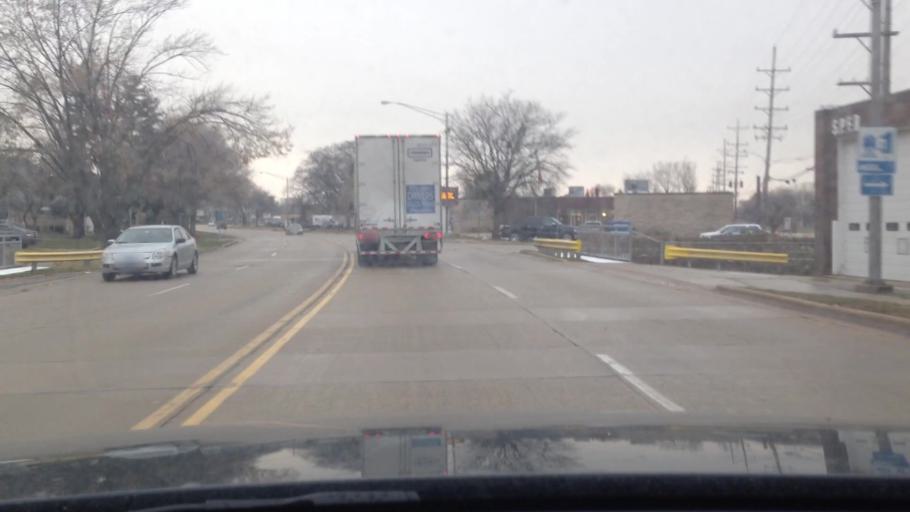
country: US
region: Illinois
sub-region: Cook County
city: Schiller Park
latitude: 41.9600
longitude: -87.8712
